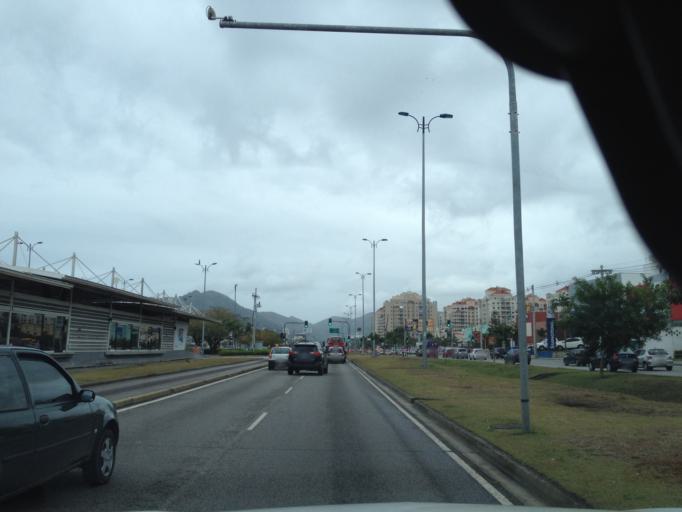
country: BR
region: Rio de Janeiro
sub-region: Nilopolis
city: Nilopolis
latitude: -23.0142
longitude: -43.4664
